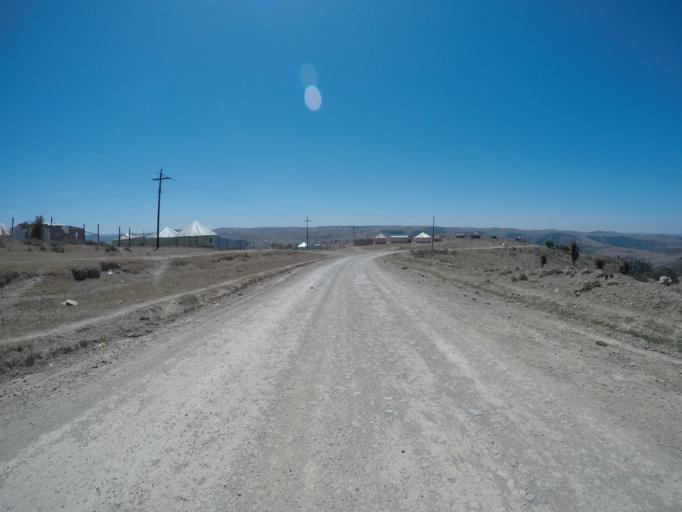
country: ZA
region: Eastern Cape
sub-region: OR Tambo District Municipality
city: Mthatha
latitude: -31.8810
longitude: 28.8748
